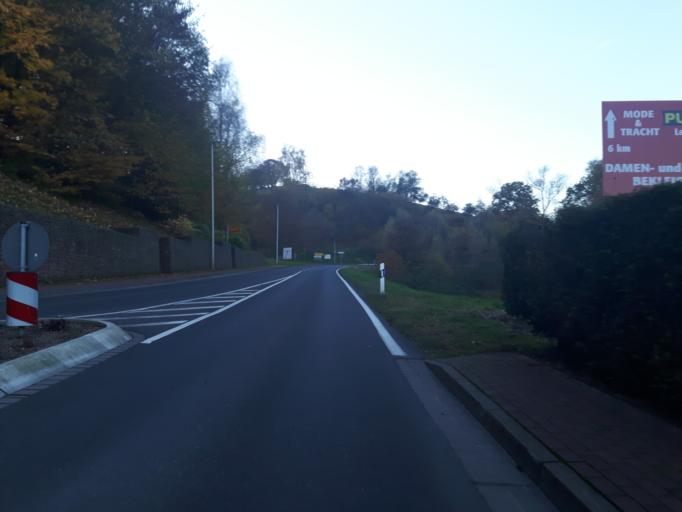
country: DE
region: Bavaria
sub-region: Regierungsbezirk Unterfranken
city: Heimbuchenthal
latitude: 49.8835
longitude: 9.2877
